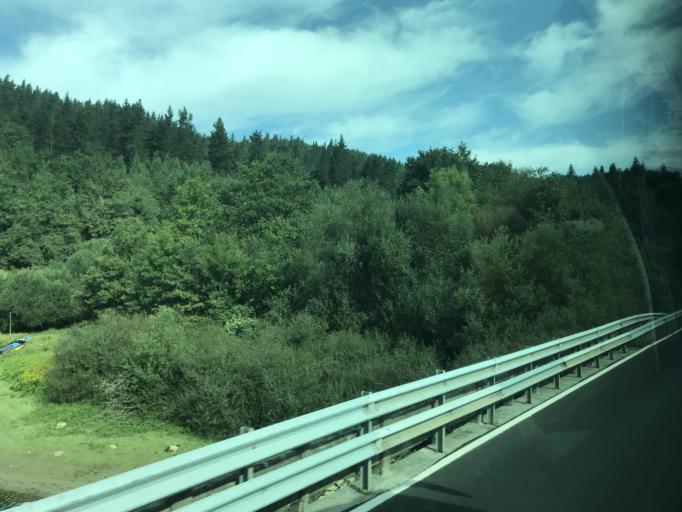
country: ES
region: Basque Country
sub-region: Bizkaia
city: Otxandio
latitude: 43.0298
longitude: -2.6513
